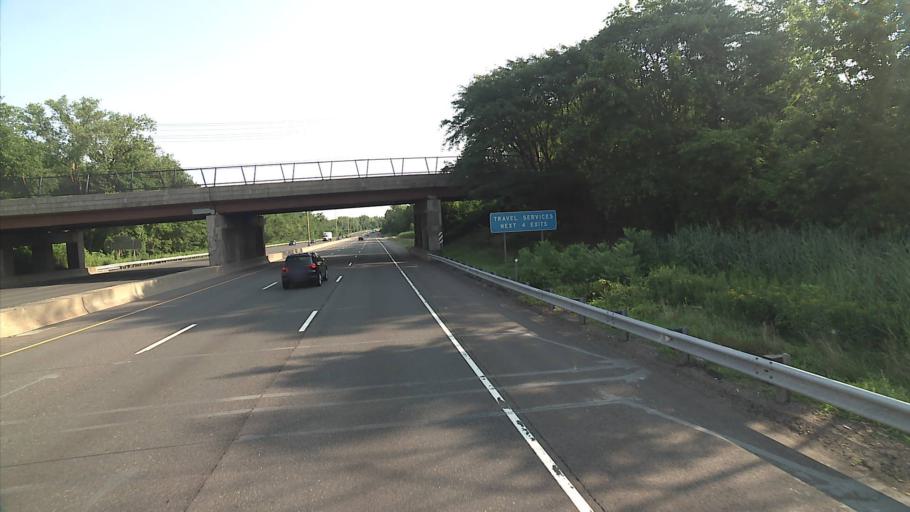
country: US
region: Connecticut
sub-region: Hartford County
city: Windsor Locks
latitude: 41.9429
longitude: -72.6062
